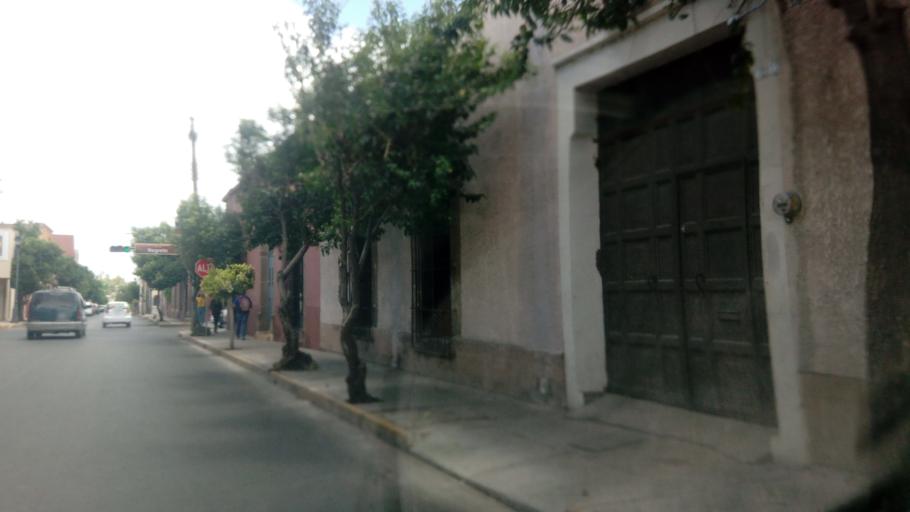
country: MX
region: Durango
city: Victoria de Durango
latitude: 24.0258
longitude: -104.6744
